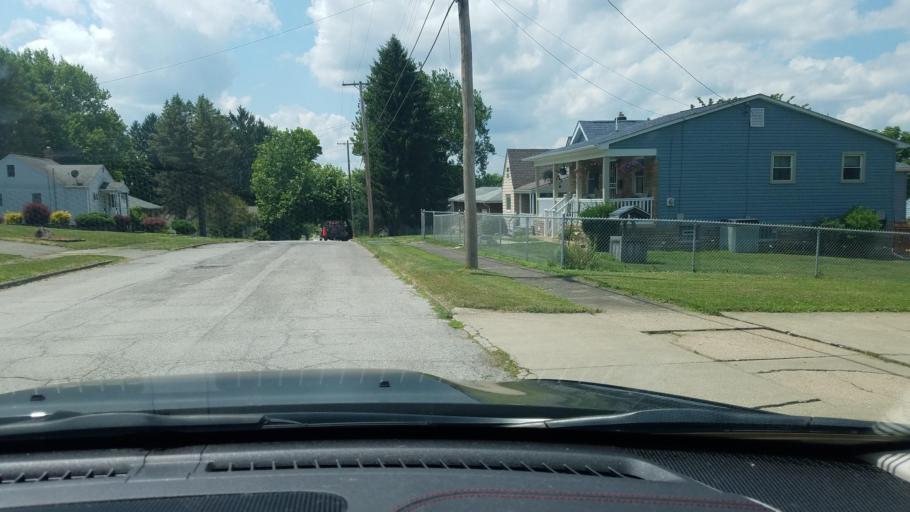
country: US
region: Ohio
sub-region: Mahoning County
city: Campbell
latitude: 41.0766
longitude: -80.5842
